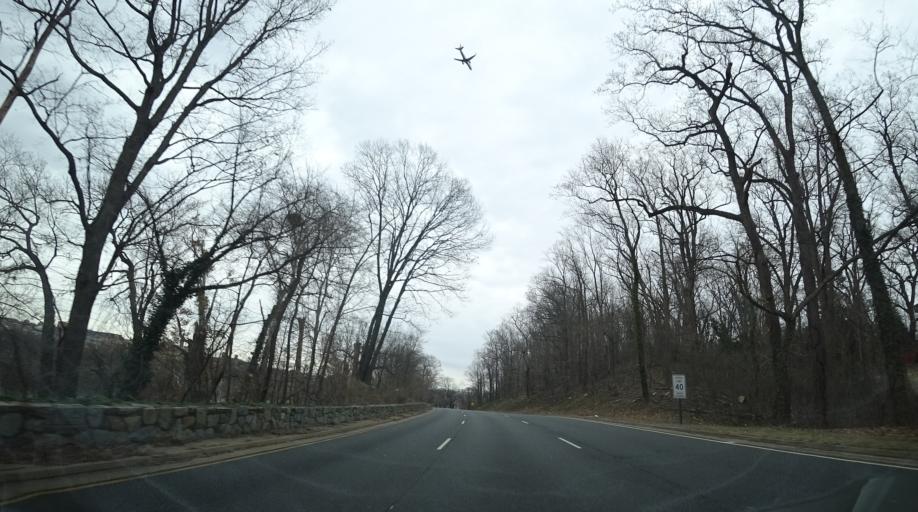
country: US
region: Virginia
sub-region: Arlington County
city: Arlington
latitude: 38.9014
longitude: -77.0812
